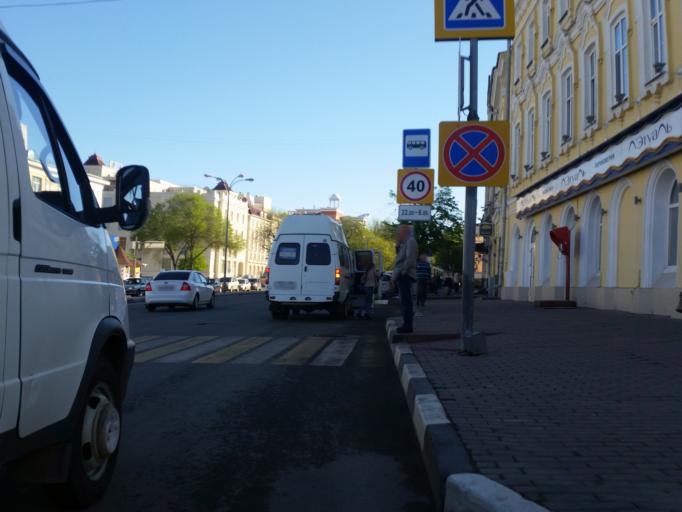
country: RU
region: Ulyanovsk
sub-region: Ulyanovskiy Rayon
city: Ulyanovsk
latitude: 54.3186
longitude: 48.3981
